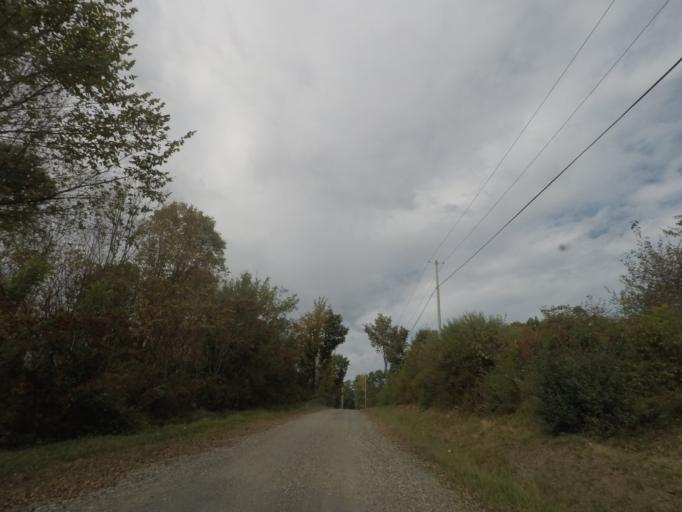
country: US
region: New York
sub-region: Rensselaer County
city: West Sand Lake
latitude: 42.5808
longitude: -73.6129
